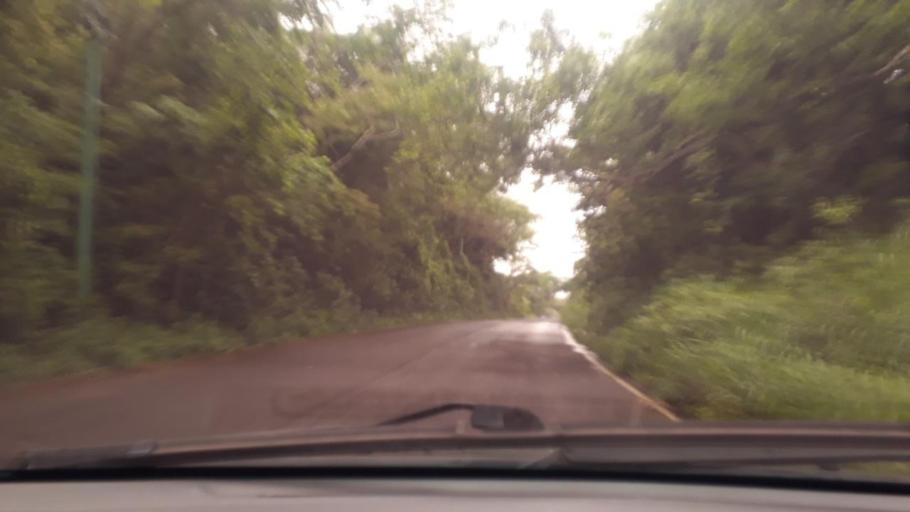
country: GT
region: Jutiapa
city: Comapa
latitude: 14.1059
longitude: -89.9646
